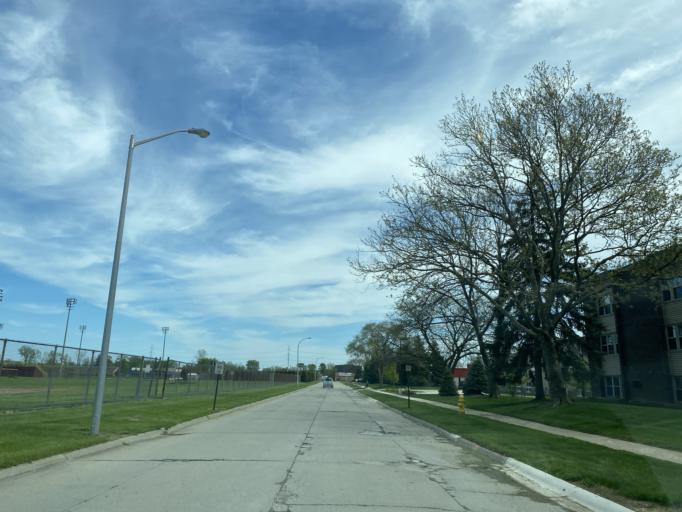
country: US
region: Michigan
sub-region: Wayne County
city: Riverview
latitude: 42.1742
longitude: -83.1779
